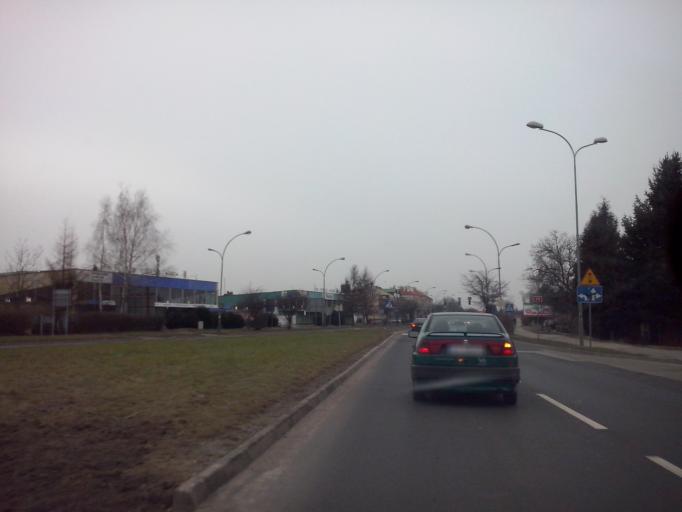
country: PL
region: Lublin Voivodeship
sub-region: Zamosc
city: Zamosc
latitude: 50.7154
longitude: 23.2279
